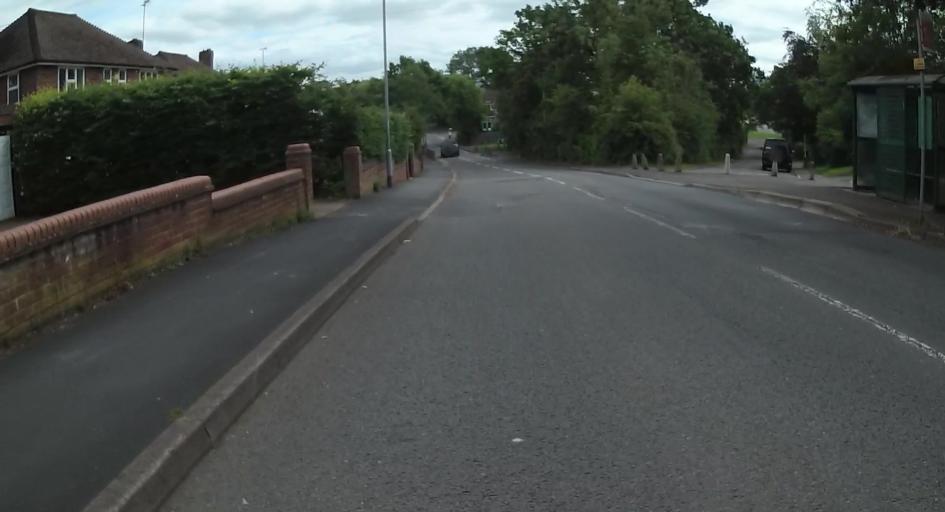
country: GB
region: England
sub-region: Wokingham
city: Earley
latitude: 51.4340
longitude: -0.9302
